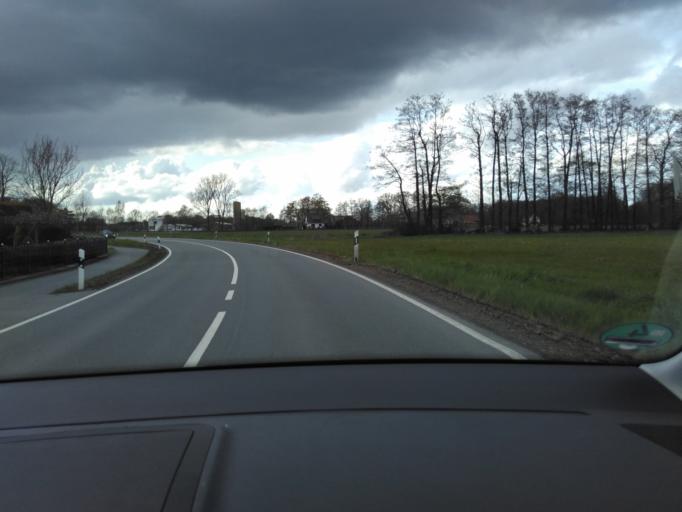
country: DE
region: North Rhine-Westphalia
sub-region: Regierungsbezirk Detmold
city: Verl
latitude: 51.9130
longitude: 8.4610
